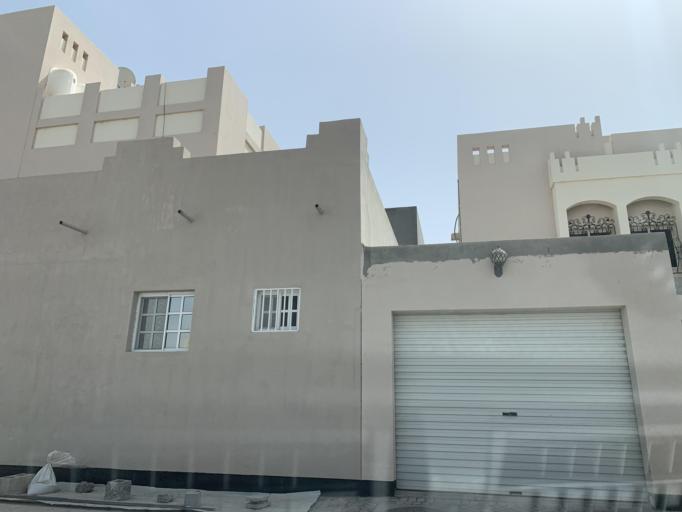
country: BH
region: Northern
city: Madinat `Isa
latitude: 26.1717
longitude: 50.5251
